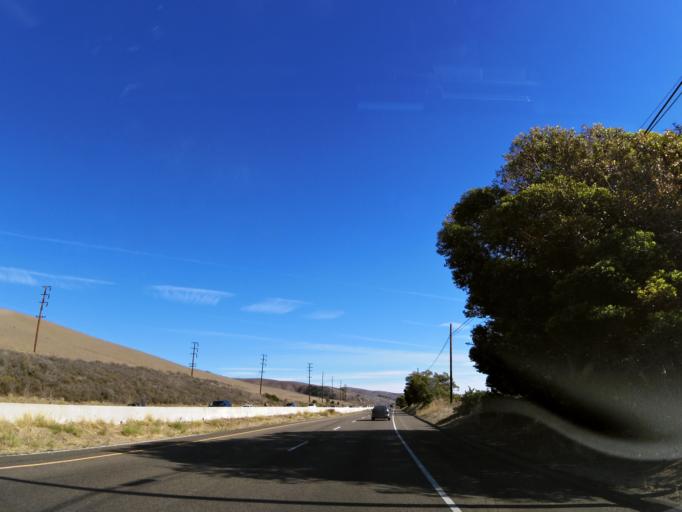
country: US
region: California
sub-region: Santa Barbara County
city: Solvang
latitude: 34.4742
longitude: -120.1523
